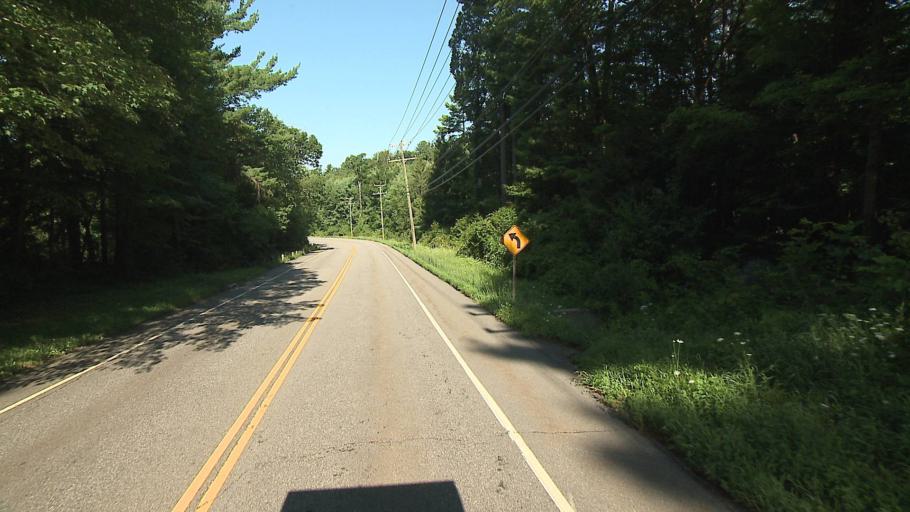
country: US
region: Connecticut
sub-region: Litchfield County
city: Litchfield
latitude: 41.8462
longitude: -73.3182
